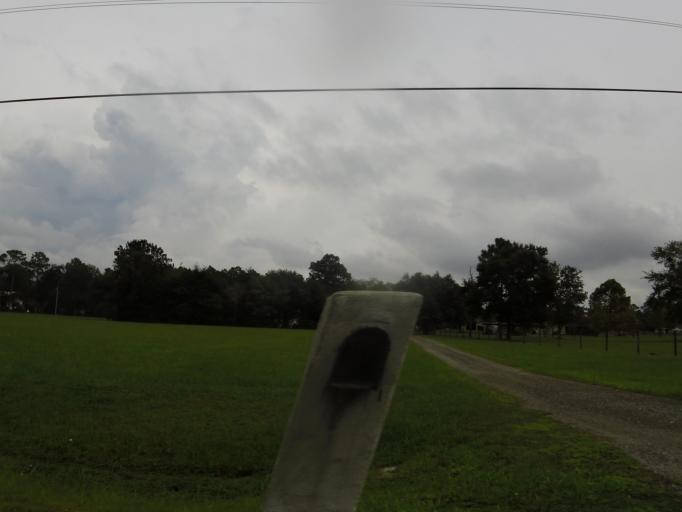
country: US
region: Florida
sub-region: Clay County
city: Middleburg
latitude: 30.1096
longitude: -81.9617
